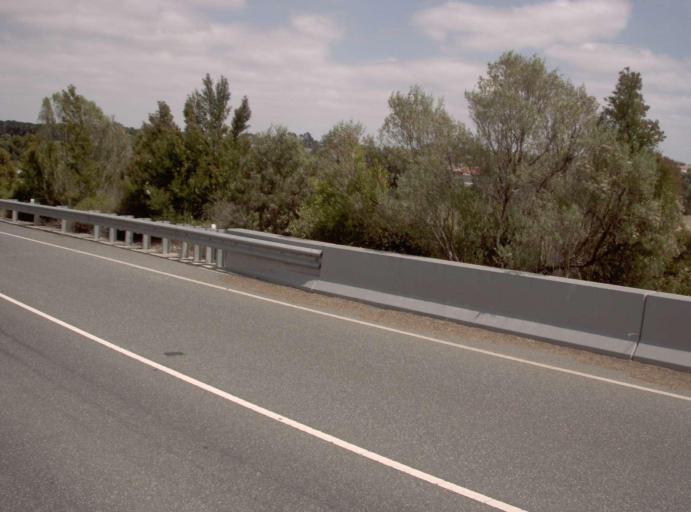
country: AU
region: Victoria
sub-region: Casey
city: Berwick
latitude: -38.0619
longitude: 145.3689
